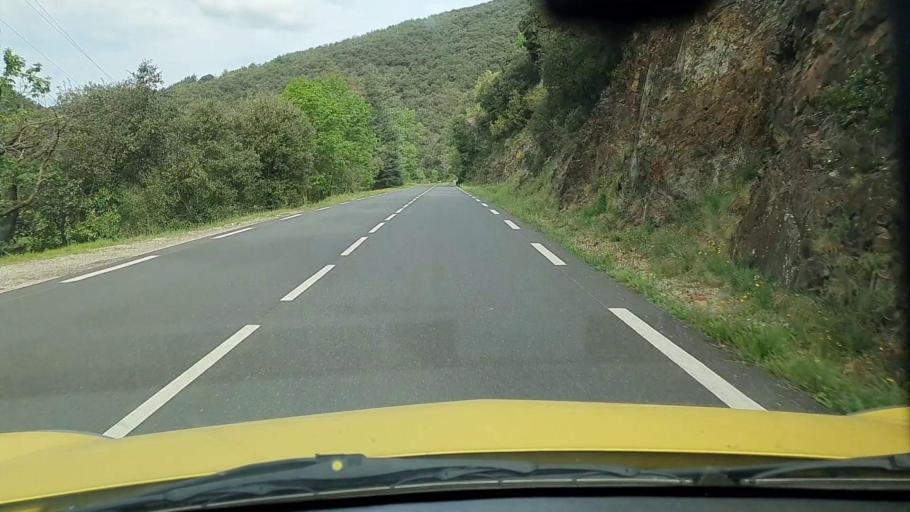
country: FR
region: Languedoc-Roussillon
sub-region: Departement du Gard
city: Valleraugue
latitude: 44.0764
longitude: 3.6675
